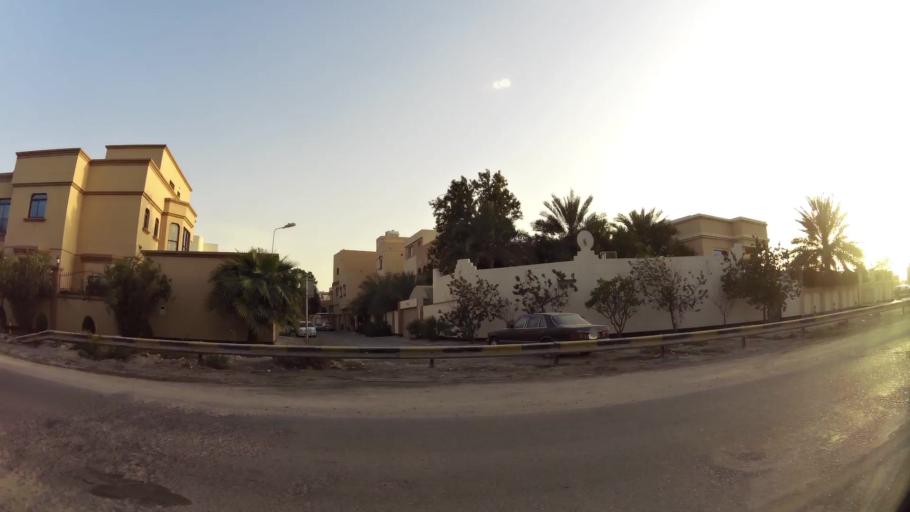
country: BH
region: Northern
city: Madinat `Isa
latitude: 26.1955
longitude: 50.4801
